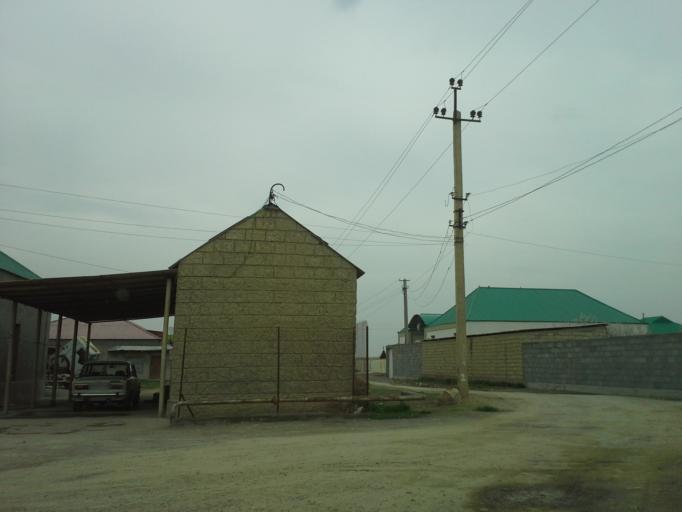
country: TM
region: Ahal
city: Abadan
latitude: 37.9732
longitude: 58.2279
